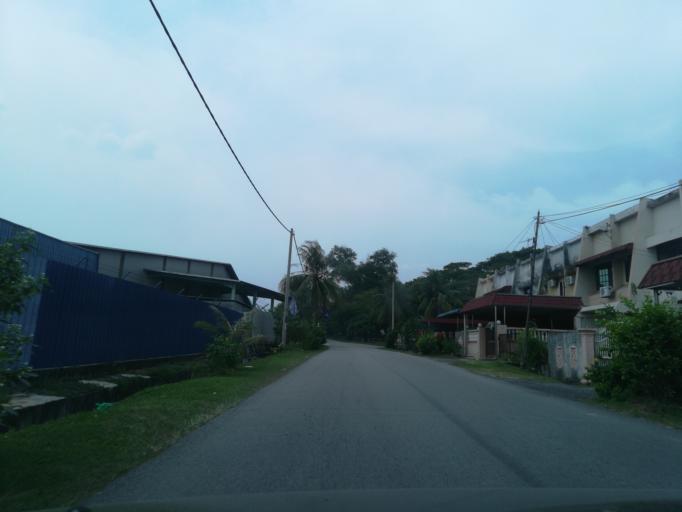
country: MY
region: Kedah
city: Kulim
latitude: 5.4013
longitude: 100.5616
